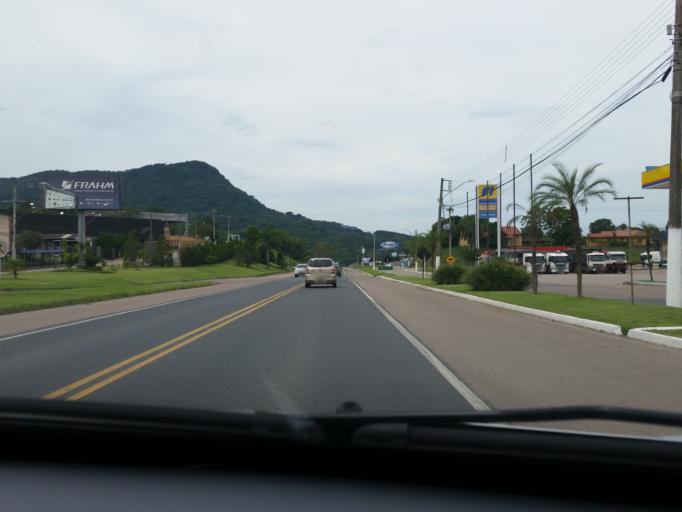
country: BR
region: Santa Catarina
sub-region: Rio Do Sul
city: Rio do Sul
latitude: -27.1970
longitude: -49.6276
